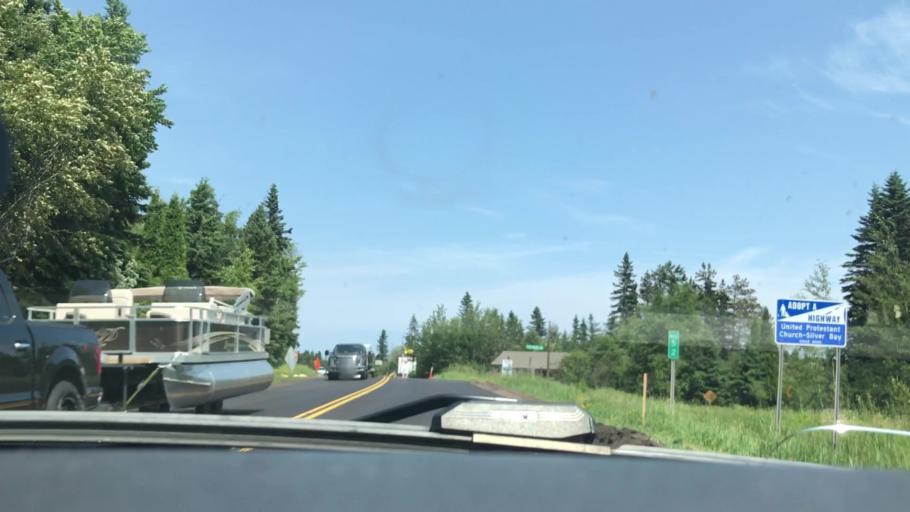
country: US
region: Minnesota
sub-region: Lake County
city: Silver Bay
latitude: 47.2679
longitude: -91.2854
